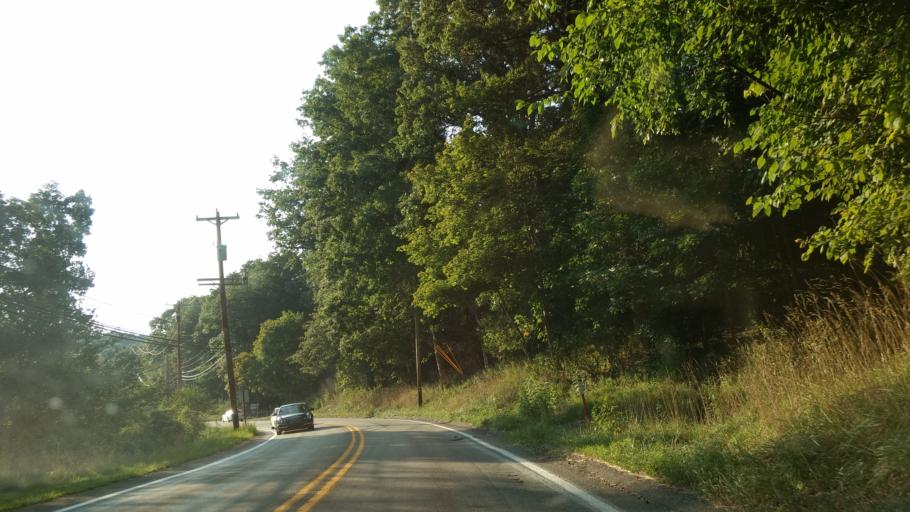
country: US
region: Pennsylvania
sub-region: Allegheny County
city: Gibsonia
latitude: 40.5957
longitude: -79.9789
